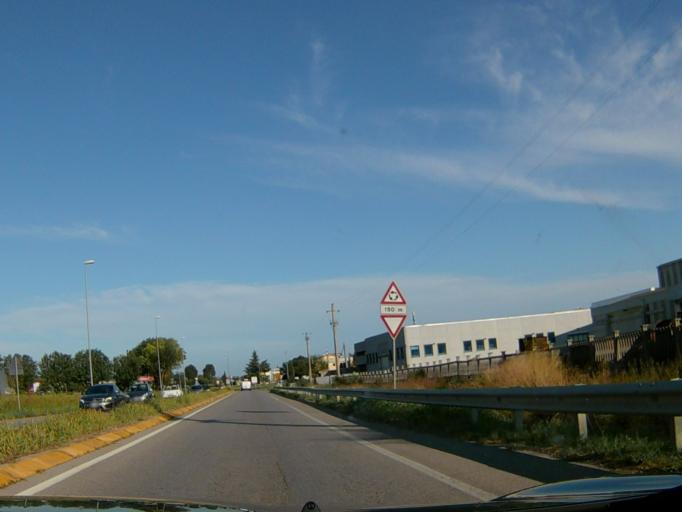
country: IT
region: Lombardy
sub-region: Provincia di Brescia
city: Ponte San Marco
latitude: 45.4714
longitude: 10.4380
